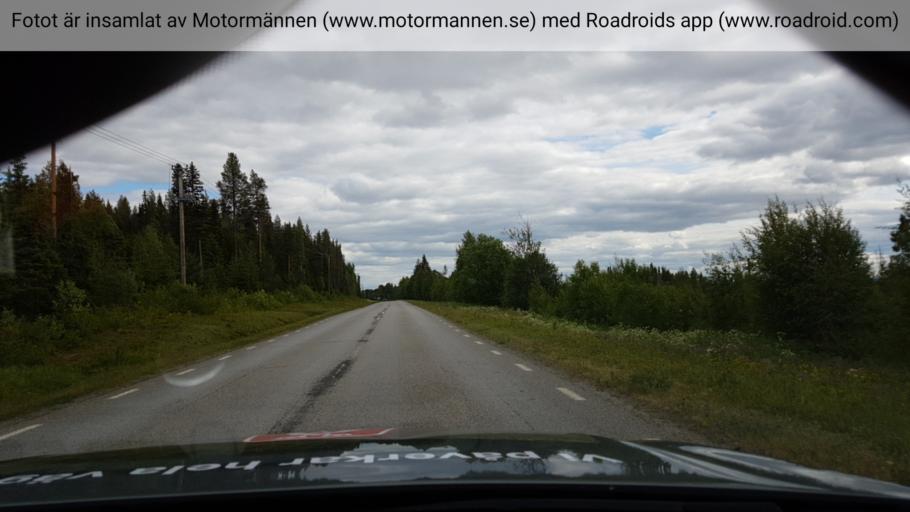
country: SE
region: Jaemtland
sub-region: Stroemsunds Kommun
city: Stroemsund
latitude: 63.9128
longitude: 15.5227
